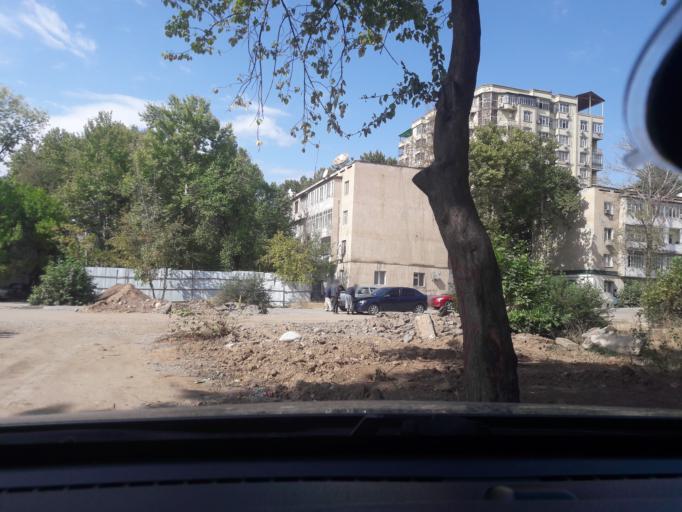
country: TJ
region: Dushanbe
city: Dushanbe
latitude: 38.5864
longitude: 68.7494
